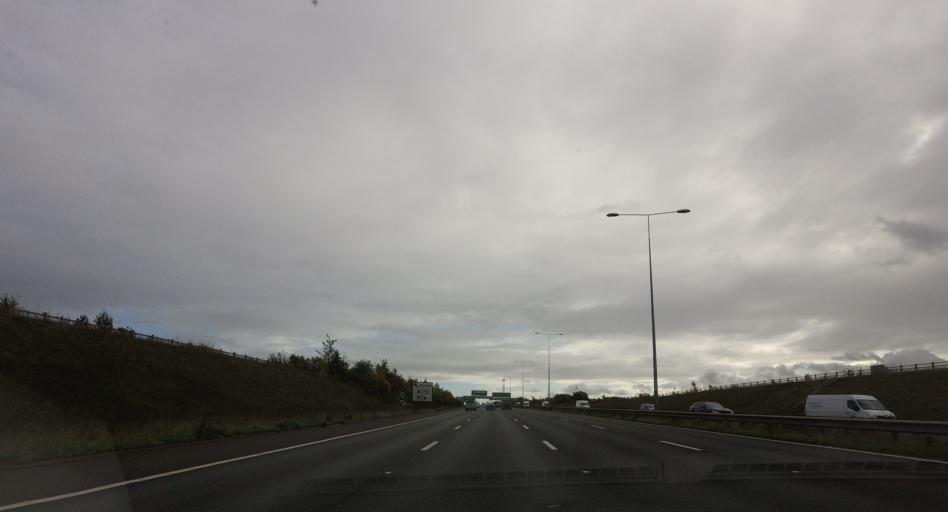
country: GB
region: England
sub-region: Kent
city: Gravesend
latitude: 51.4199
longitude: 0.3455
